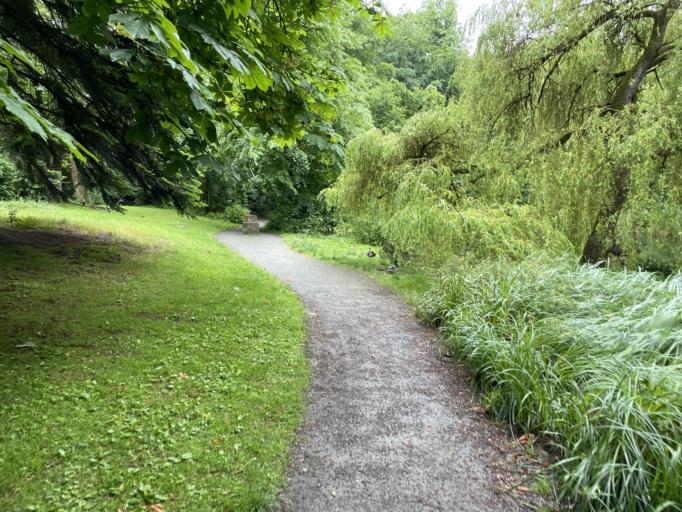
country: DE
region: Lower Saxony
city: Cuxhaven
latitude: 53.8568
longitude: 8.6993
